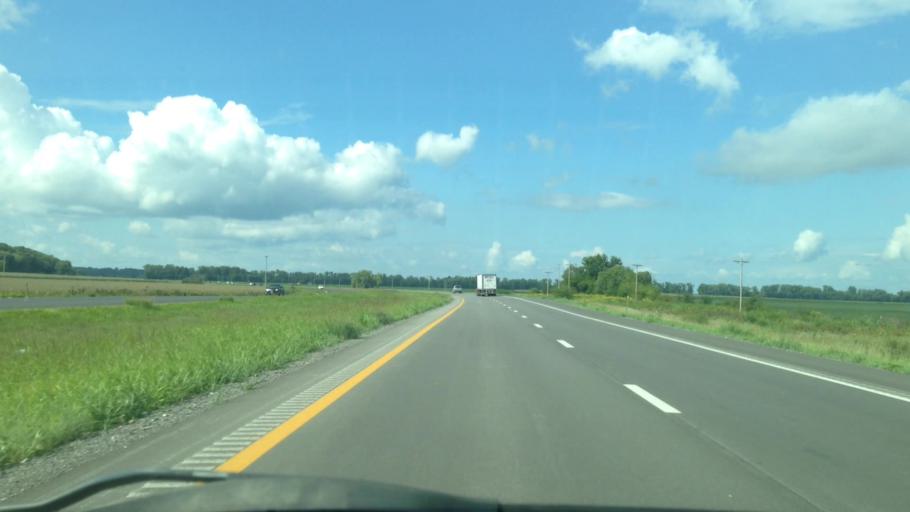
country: US
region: Illinois
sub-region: Adams County
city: Quincy
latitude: 39.9654
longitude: -91.5181
